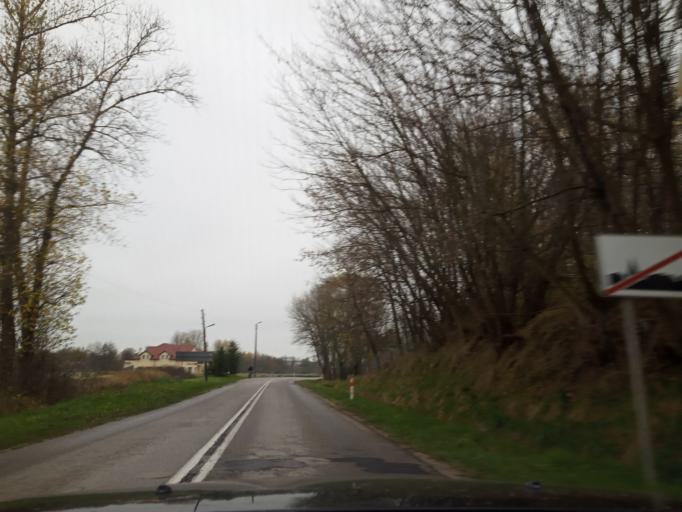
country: PL
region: Swietokrzyskie
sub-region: Powiat pinczowski
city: Dzialoszyce
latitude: 50.3676
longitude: 20.3461
